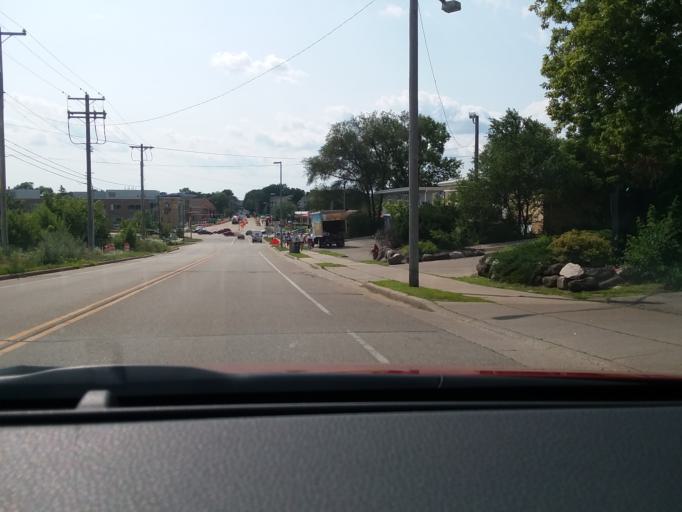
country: US
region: Wisconsin
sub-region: Dane County
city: Madison
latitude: 43.0385
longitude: -89.3918
